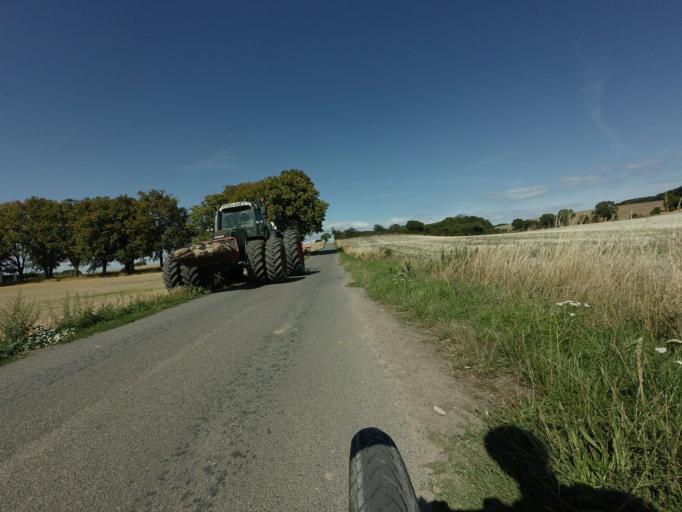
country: DK
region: Zealand
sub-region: Vordingborg Kommune
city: Stege
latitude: 55.0139
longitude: 12.4596
